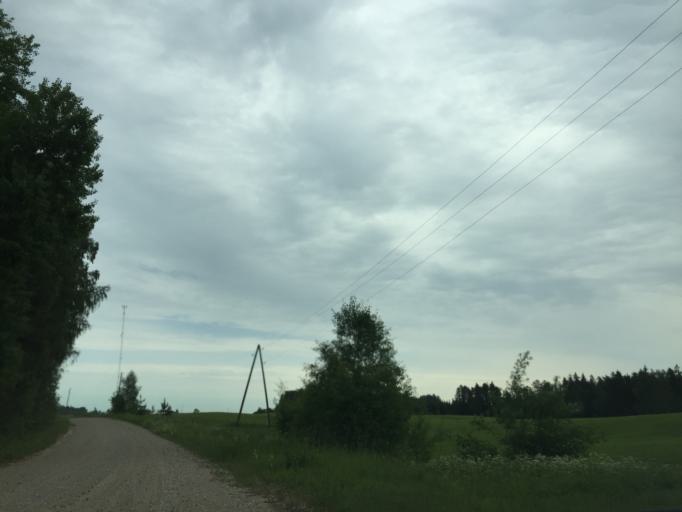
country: LV
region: Tukuma Rajons
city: Tukums
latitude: 57.0392
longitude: 23.0953
